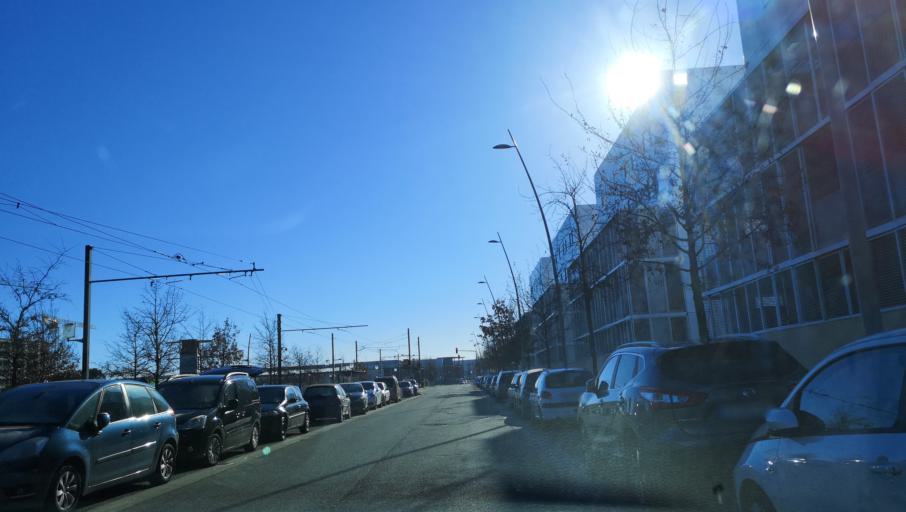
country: FR
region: Midi-Pyrenees
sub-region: Departement de la Haute-Garonne
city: Beauzelle
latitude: 43.6556
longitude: 1.3727
